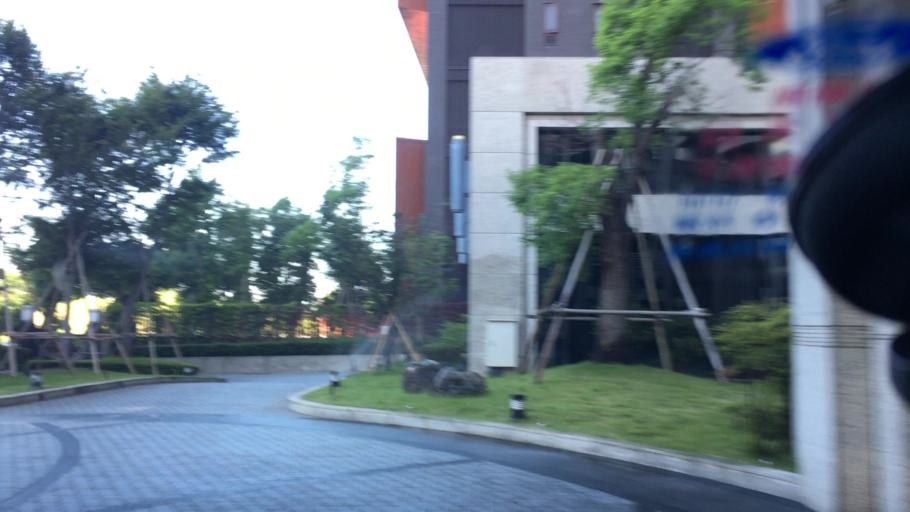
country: TW
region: Taiwan
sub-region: Hsinchu
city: Zhubei
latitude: 24.8194
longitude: 121.0096
